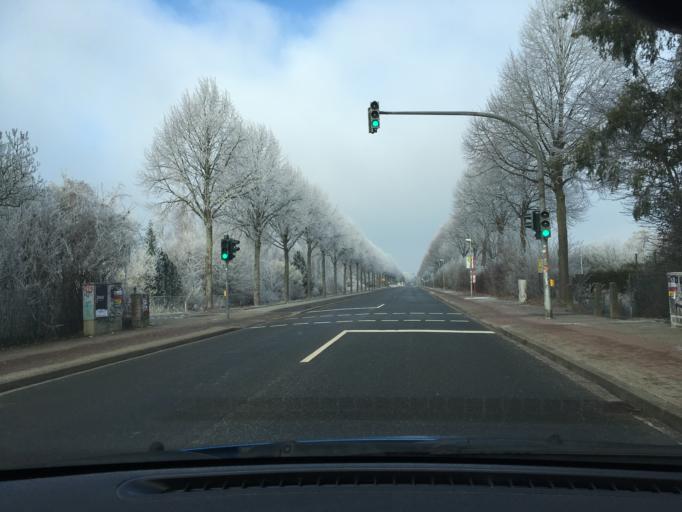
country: DE
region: Lower Saxony
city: Lueneburg
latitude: 53.2609
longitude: 10.3912
